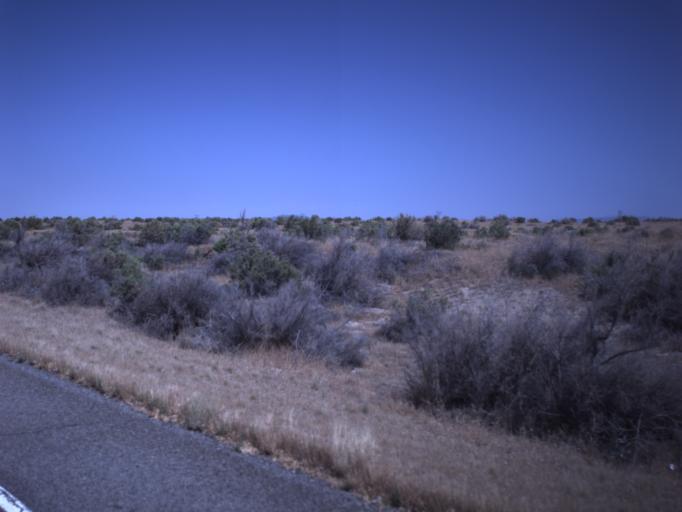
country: US
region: Utah
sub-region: Millard County
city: Delta
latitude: 39.4748
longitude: -112.4823
